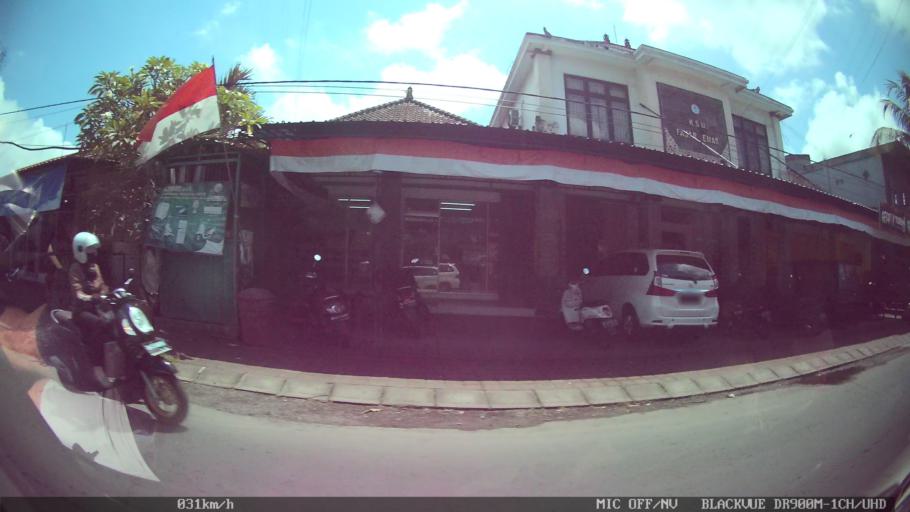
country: ID
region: Bali
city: Banjar Jabejero
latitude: -8.5926
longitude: 115.2553
